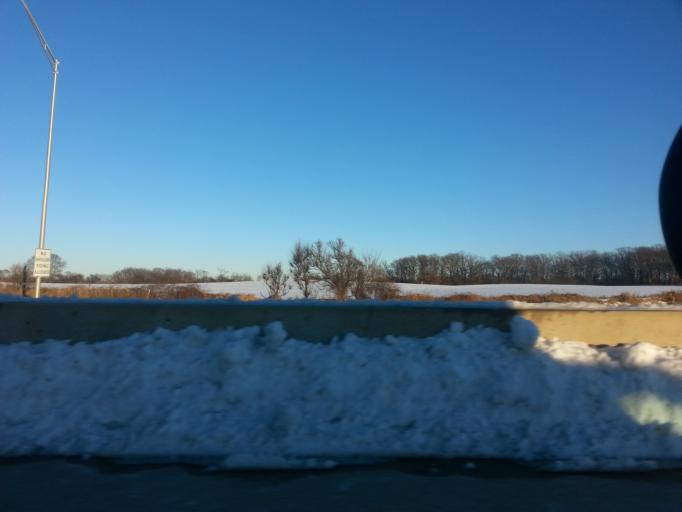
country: US
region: Illinois
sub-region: Lake County
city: Wadsworth
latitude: 42.4605
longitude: -87.9623
